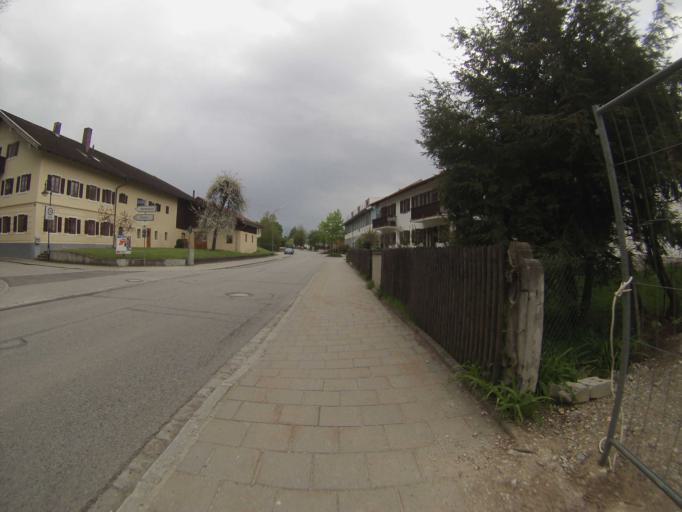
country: DE
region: Bavaria
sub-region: Upper Bavaria
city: Sauerlach
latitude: 47.9716
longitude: 11.6470
